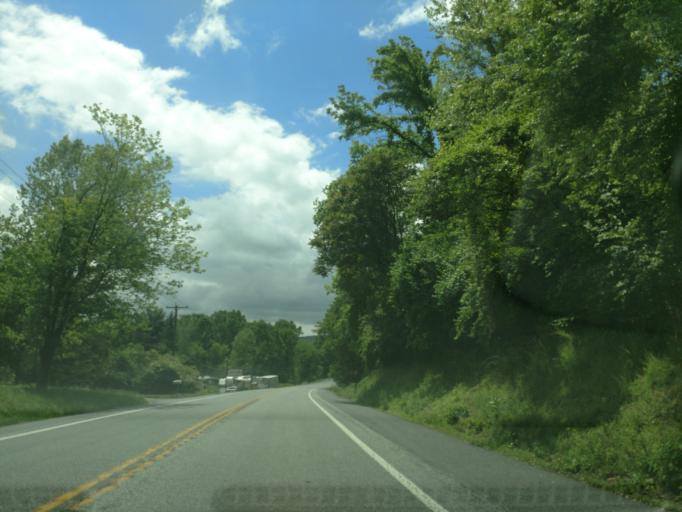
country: US
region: Pennsylvania
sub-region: Lebanon County
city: Cornwall
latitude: 40.2919
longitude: -76.4249
